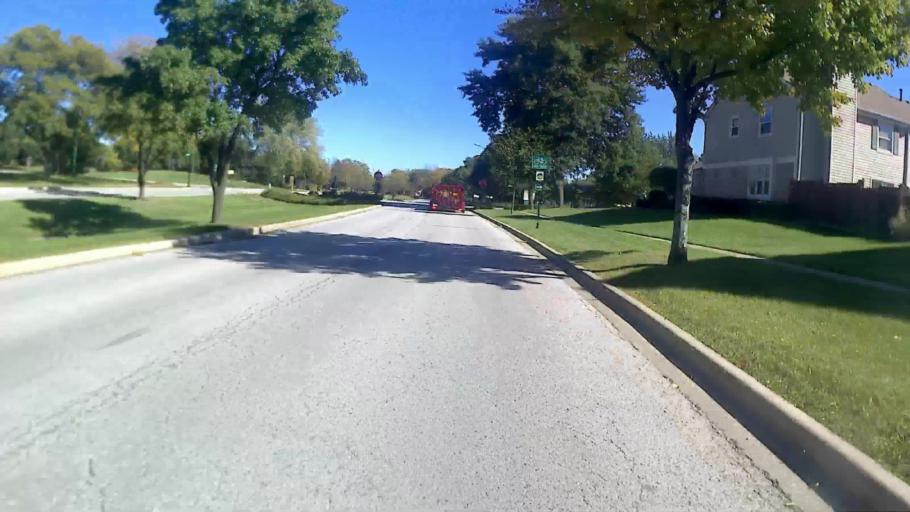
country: US
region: Illinois
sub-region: Cook County
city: Elk Grove Village
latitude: 42.0064
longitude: -87.9905
